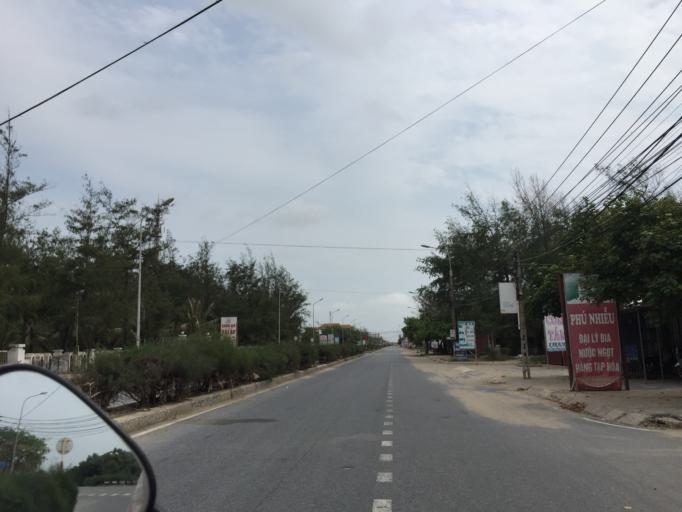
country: VN
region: Ninh Binh
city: Thi Tran Phat Diem
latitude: 20.0239
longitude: 106.2181
